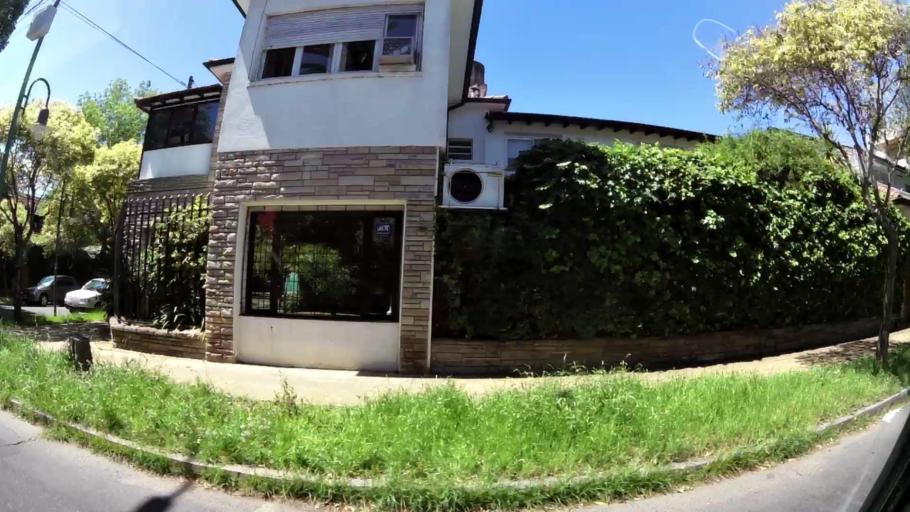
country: AR
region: Buenos Aires
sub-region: Partido de Vicente Lopez
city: Olivos
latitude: -34.5035
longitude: -58.4894
